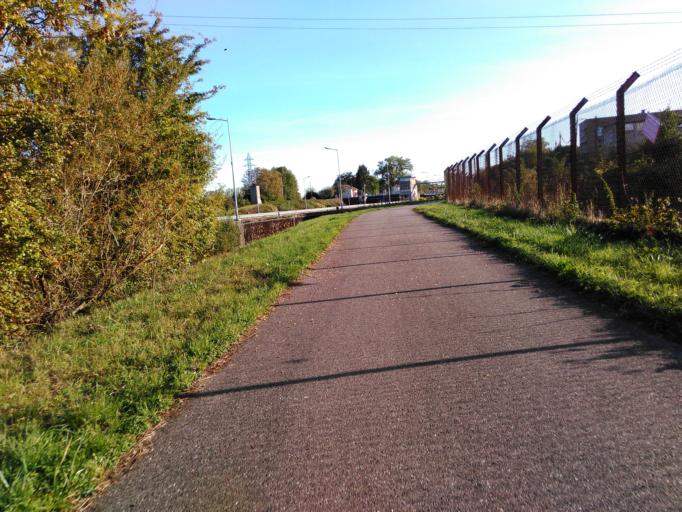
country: FR
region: Lorraine
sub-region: Departement de la Moselle
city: Bousse
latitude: 49.2837
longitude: 6.1816
